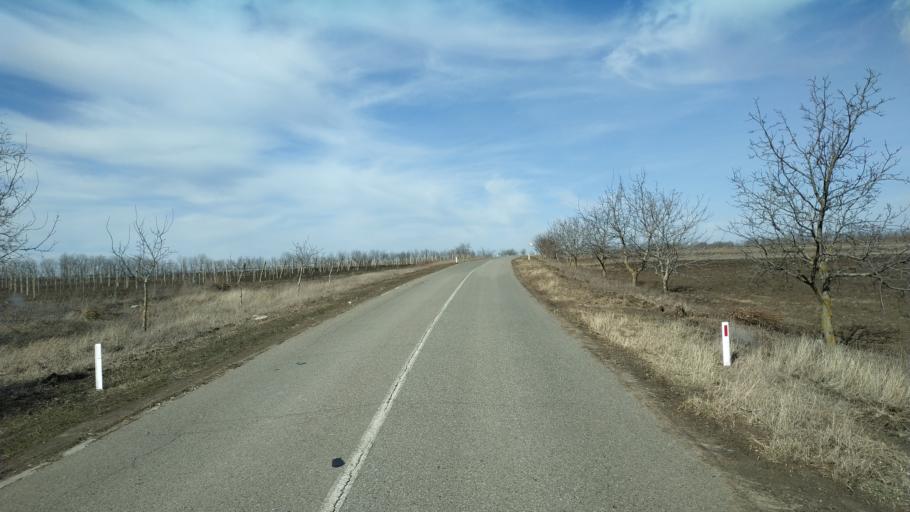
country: MD
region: Nisporeni
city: Nisporeni
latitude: 46.9412
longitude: 28.2444
